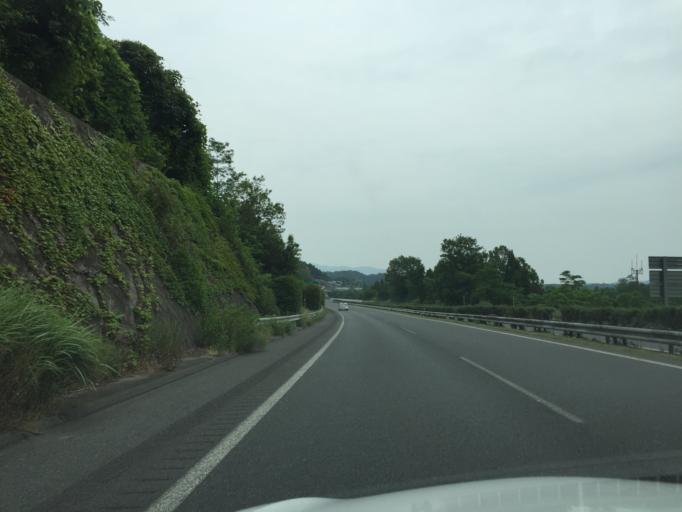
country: JP
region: Fukushima
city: Iwaki
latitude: 37.0584
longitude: 140.8306
